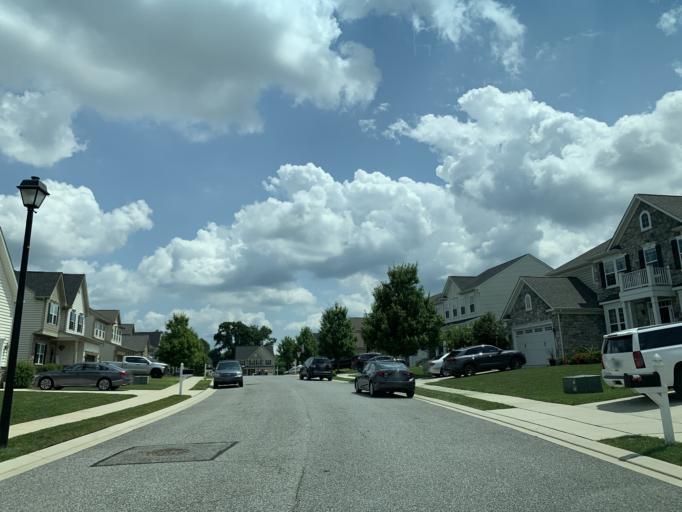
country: US
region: Maryland
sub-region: Harford County
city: Bel Air North
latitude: 39.5590
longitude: -76.3566
